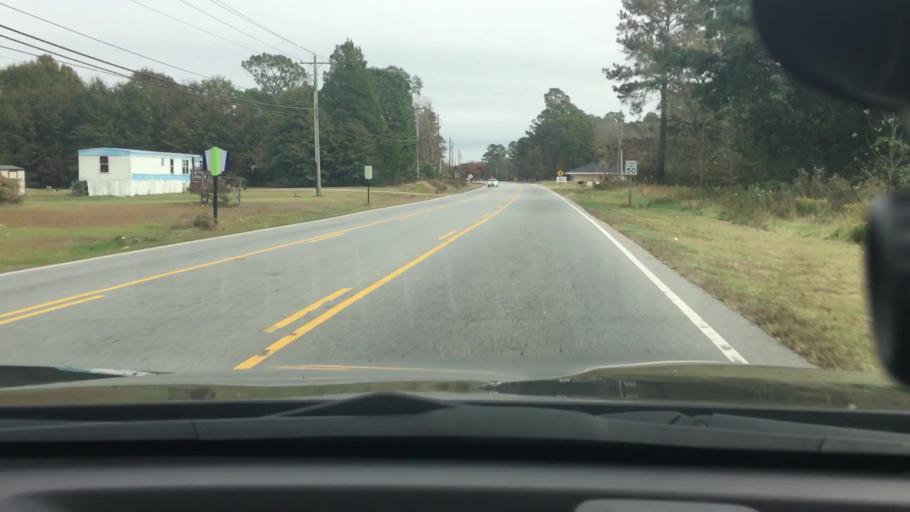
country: US
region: North Carolina
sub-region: Pitt County
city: Greenville
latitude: 35.6274
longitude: -77.3427
